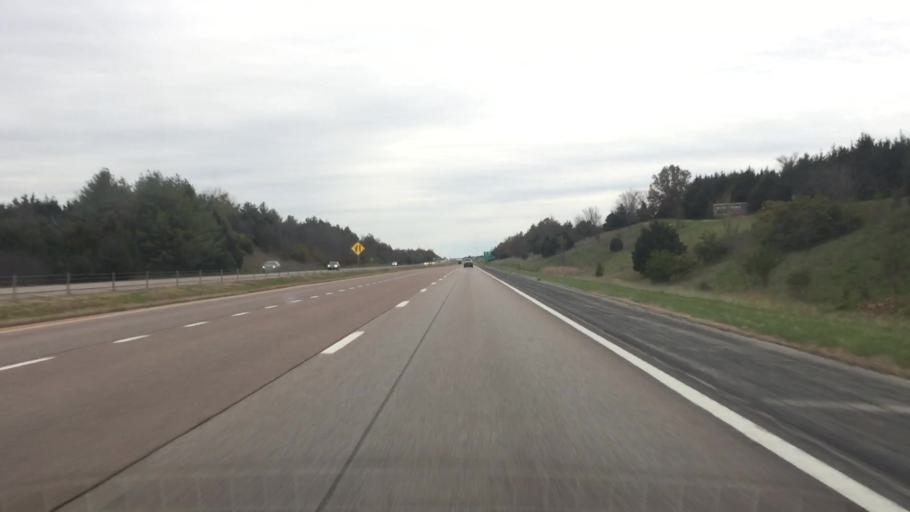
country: US
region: Missouri
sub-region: Boone County
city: Ashland
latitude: 38.7527
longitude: -92.2530
